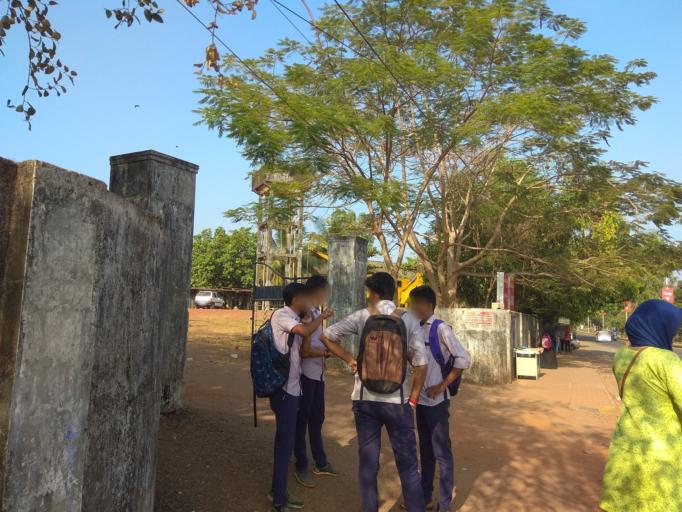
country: IN
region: Karnataka
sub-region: Dakshina Kannada
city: Mangalore
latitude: 12.8910
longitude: 74.8549
